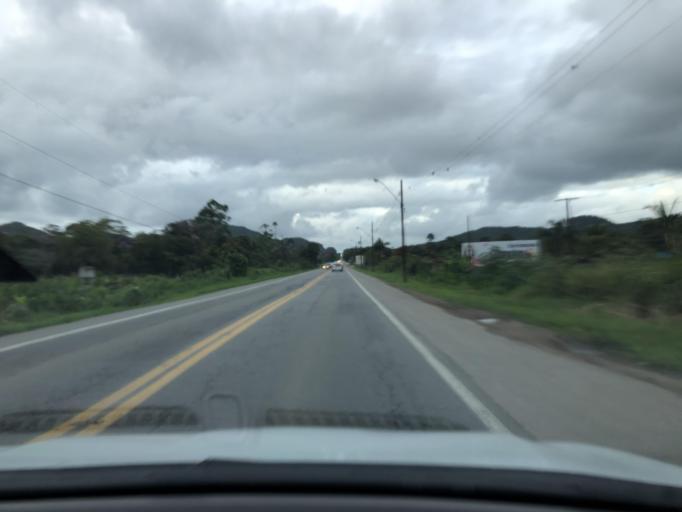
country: BR
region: Santa Catarina
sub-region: Sao Francisco Do Sul
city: Sao Francisco do Sul
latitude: -26.3356
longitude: -48.6537
